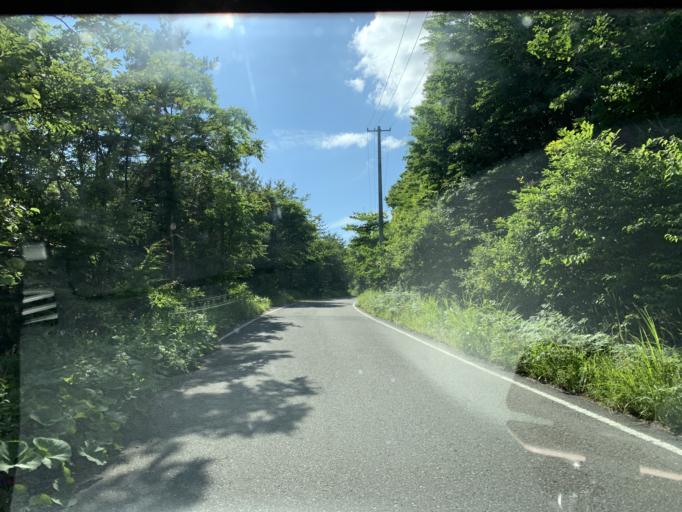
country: JP
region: Iwate
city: Ichinoseki
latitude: 38.9007
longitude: 140.8793
